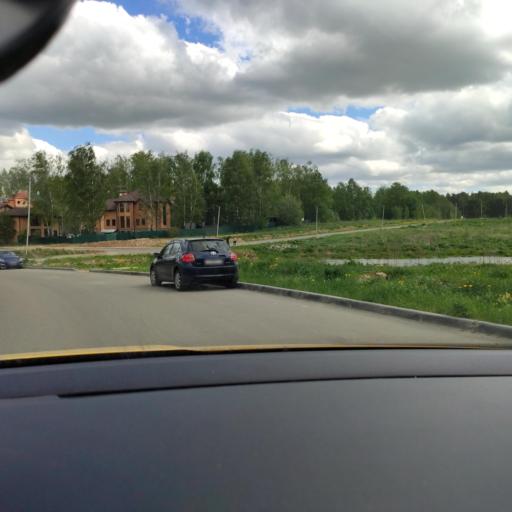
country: RU
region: Moskovskaya
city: Kommunarka
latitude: 55.5523
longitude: 37.5155
